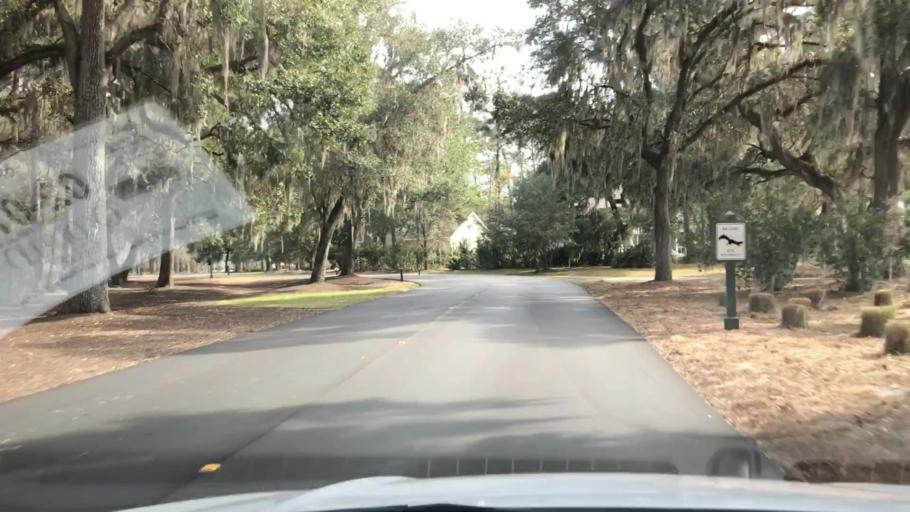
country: US
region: South Carolina
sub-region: Beaufort County
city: Bluffton
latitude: 32.3424
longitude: -80.9179
